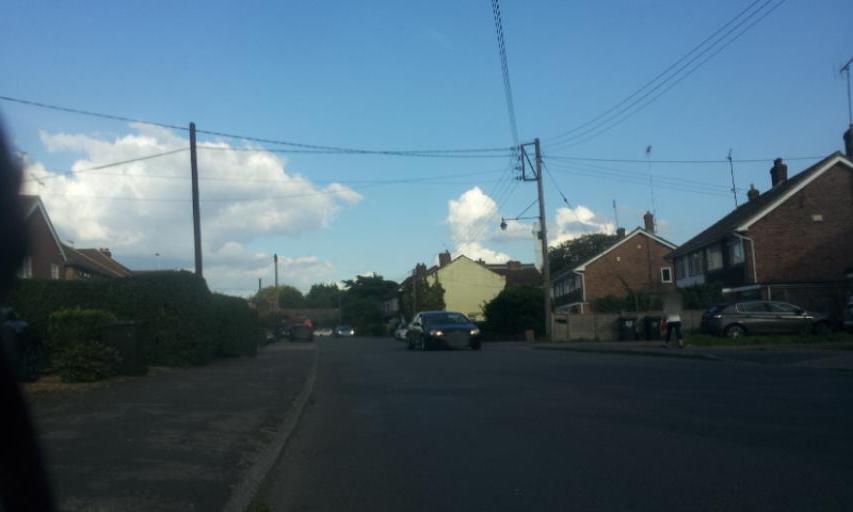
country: GB
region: England
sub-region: Kent
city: Dartford
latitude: 51.4037
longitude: 0.2413
